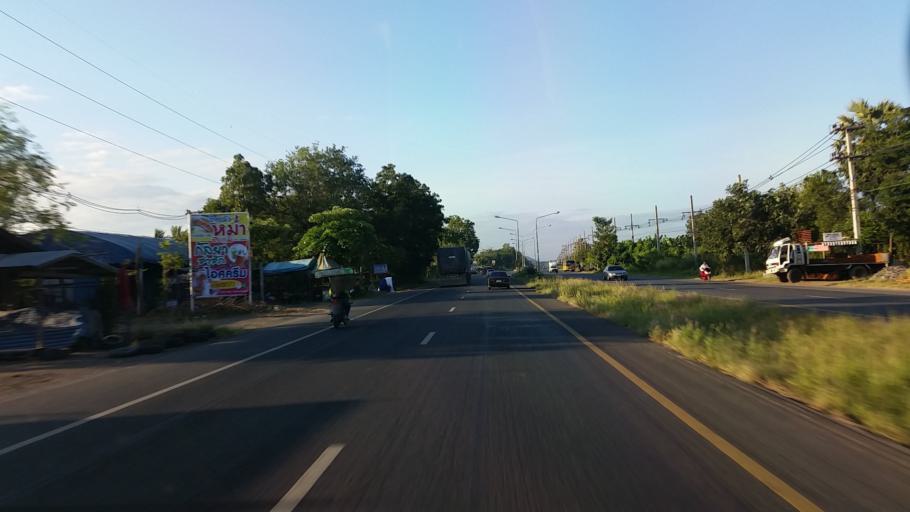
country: TH
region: Lop Buri
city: Chai Badan
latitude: 15.1888
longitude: 101.0780
